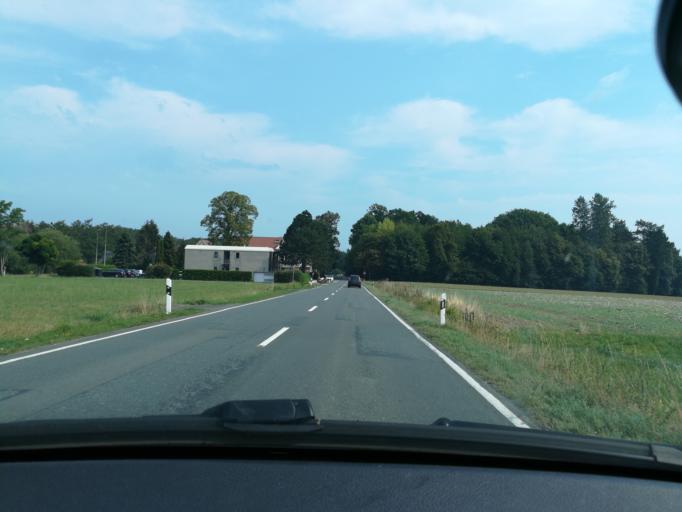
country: DE
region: North Rhine-Westphalia
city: Borgholzhausen
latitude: 52.1224
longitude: 8.3190
